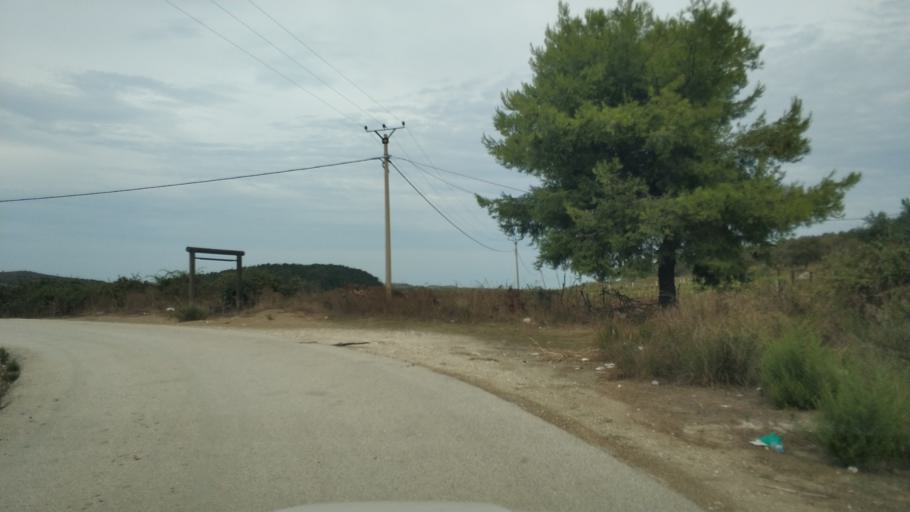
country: AL
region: Vlore
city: Vlore
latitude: 40.5128
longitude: 19.4095
